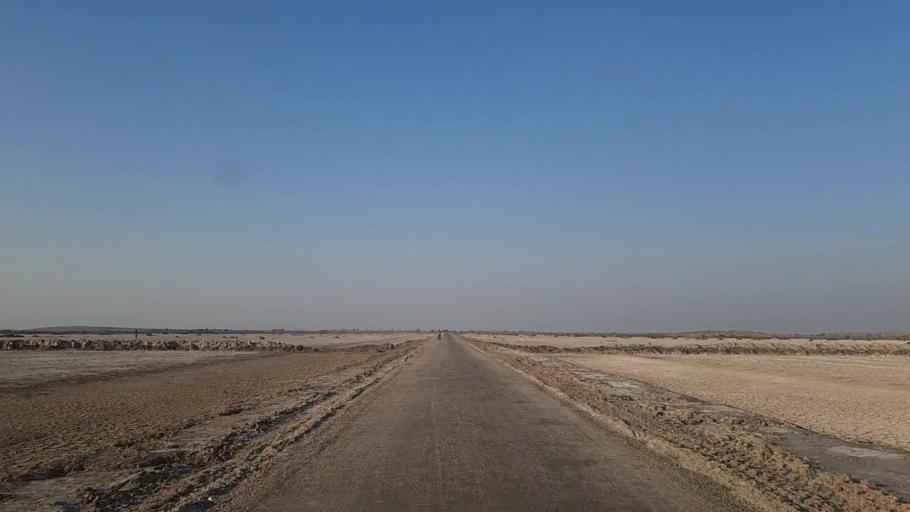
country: PK
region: Sindh
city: Jam Sahib
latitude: 26.3126
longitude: 68.6688
